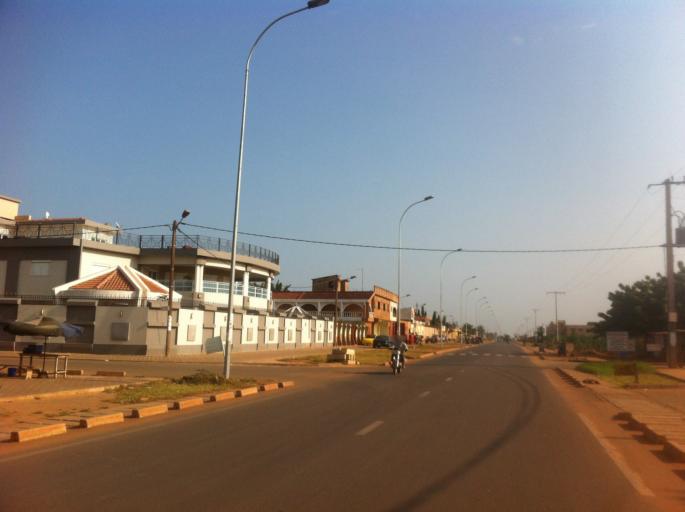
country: TG
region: Maritime
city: Lome
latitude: 6.2174
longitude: 1.1977
